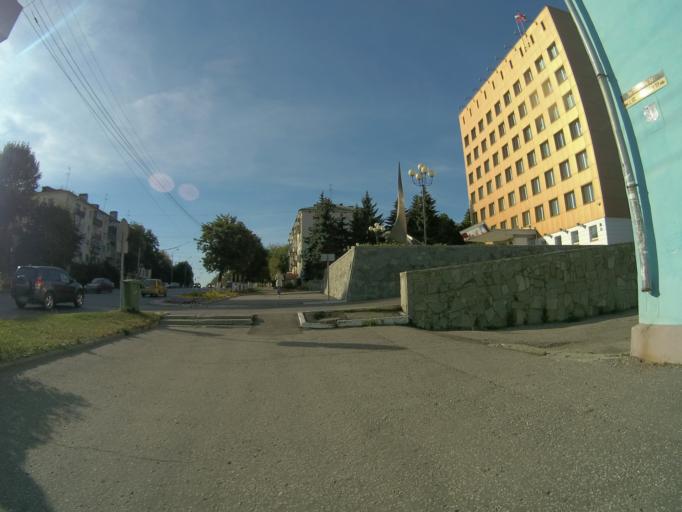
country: RU
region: Vladimir
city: Vladimir
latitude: 56.1389
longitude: 40.3994
